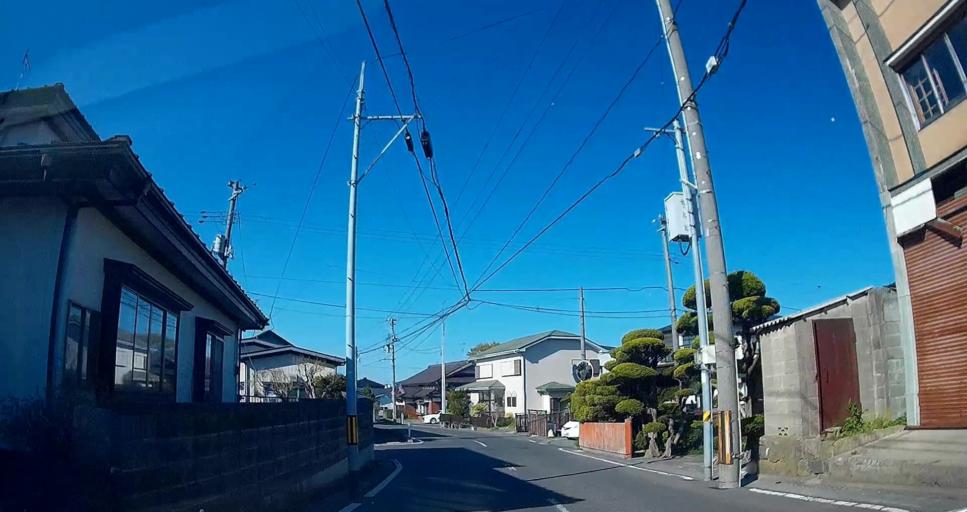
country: JP
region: Aomori
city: Hachinohe
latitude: 40.5251
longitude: 141.5482
